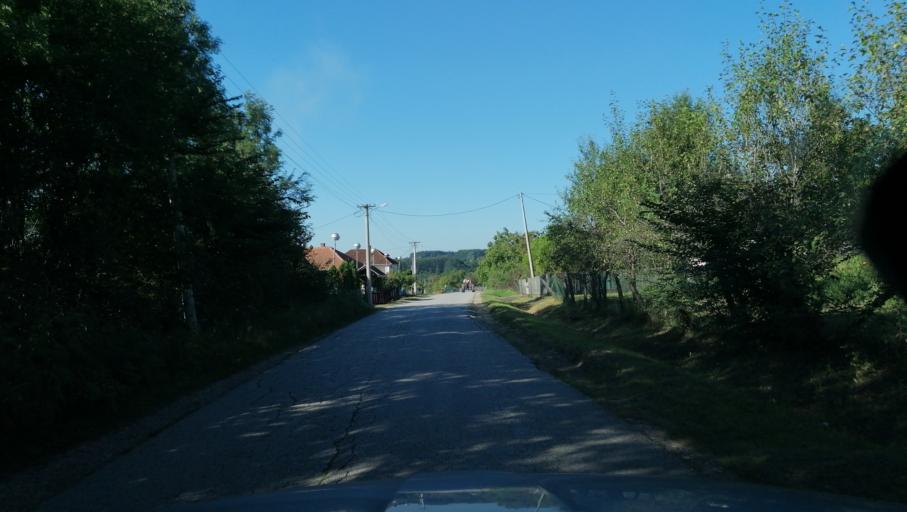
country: RS
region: Central Serbia
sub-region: Sumadijski Okrug
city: Knic
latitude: 43.8776
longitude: 20.6123
